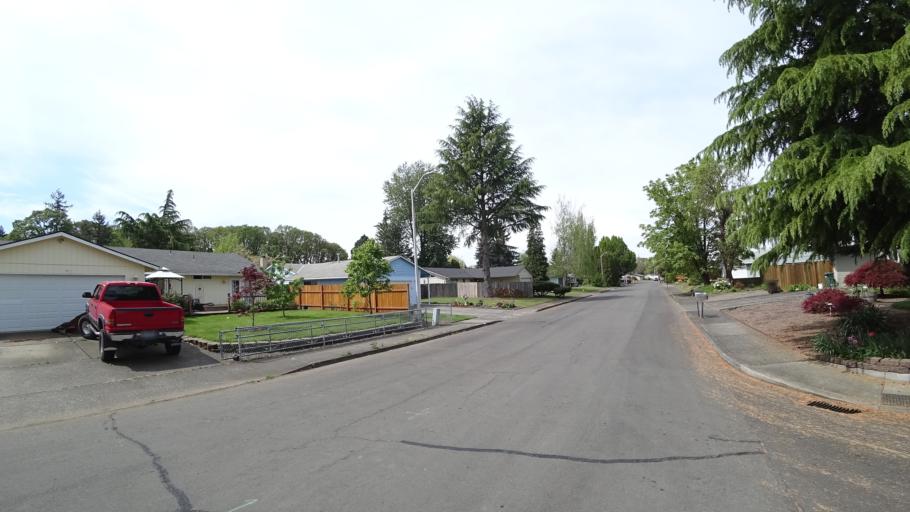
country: US
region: Oregon
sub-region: Washington County
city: Hillsboro
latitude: 45.5287
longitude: -122.9591
